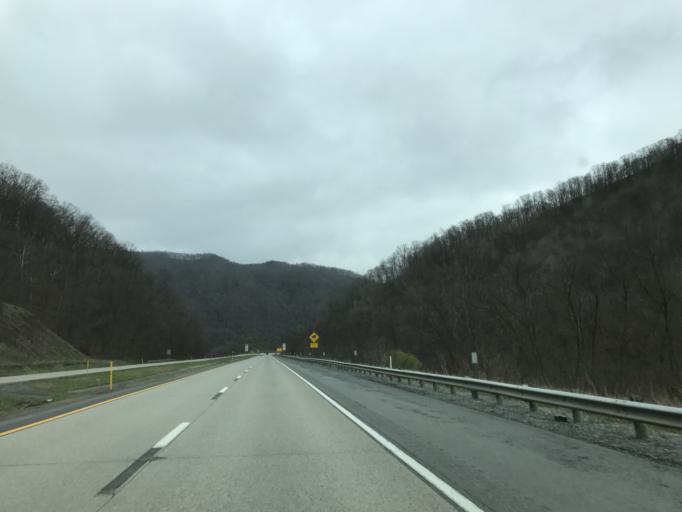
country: US
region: West Virginia
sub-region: Summers County
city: Hinton
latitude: 37.7810
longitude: -80.9236
